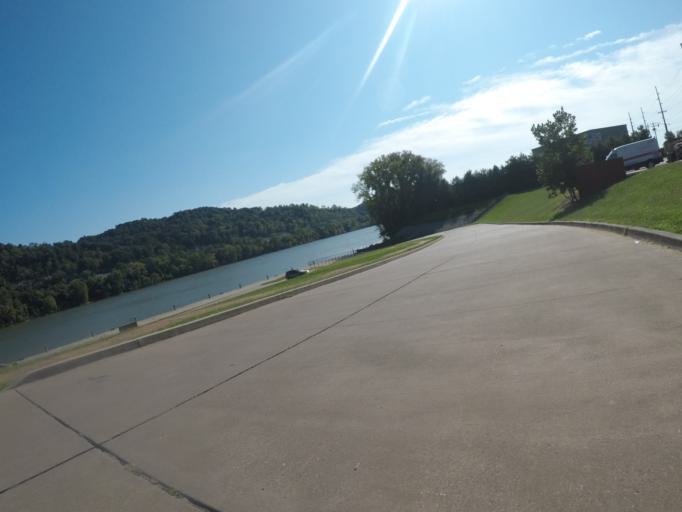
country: US
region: Kentucky
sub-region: Boyd County
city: Ashland
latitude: 38.4813
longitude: -82.6388
